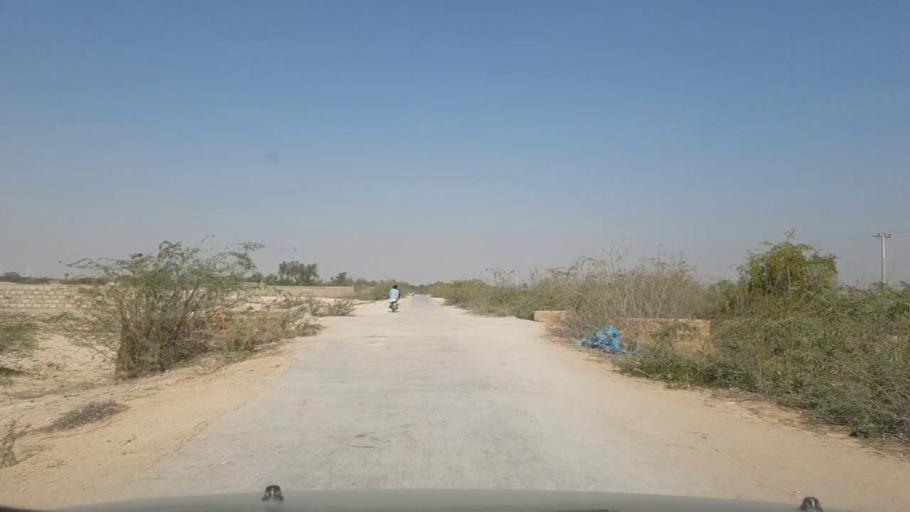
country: PK
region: Sindh
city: Daro Mehar
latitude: 25.0102
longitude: 68.0148
